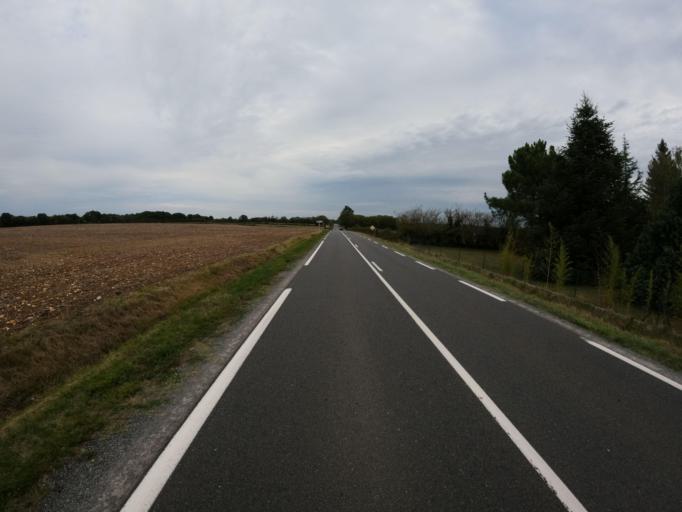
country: FR
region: Poitou-Charentes
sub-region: Departement de la Vienne
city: Lussac-les-Chateaux
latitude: 46.4031
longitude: 0.7764
